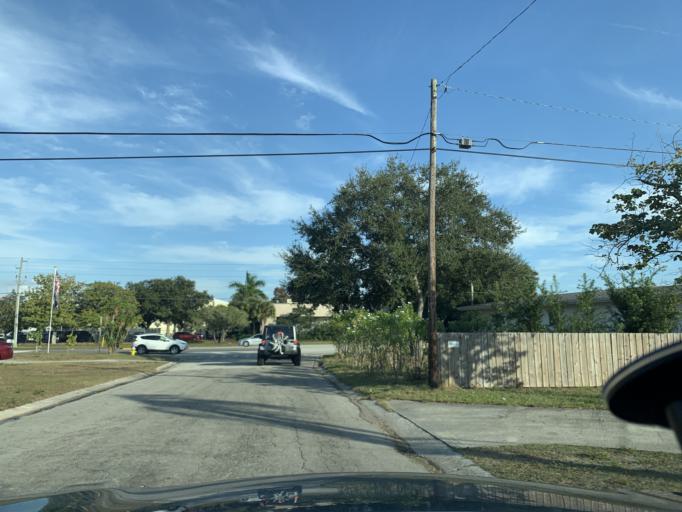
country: US
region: Florida
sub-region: Pinellas County
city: Ridgecrest
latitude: 27.9007
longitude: -82.7960
